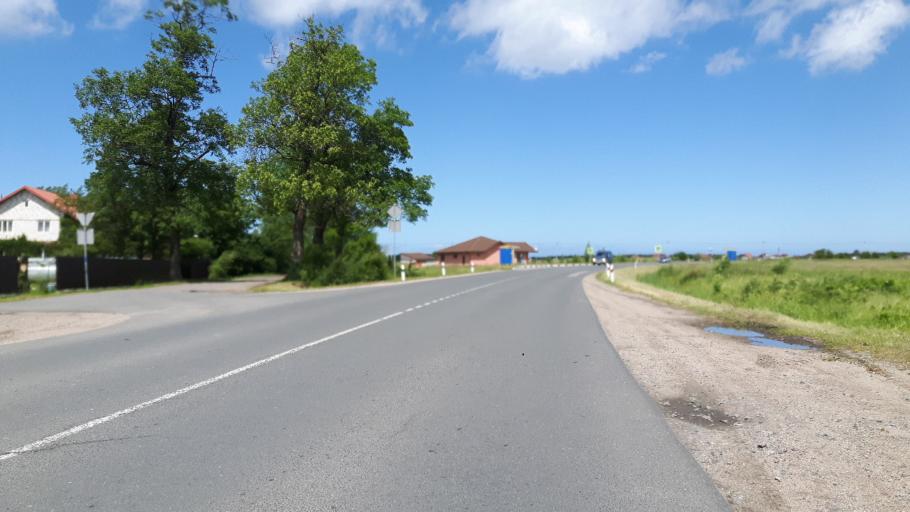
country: RU
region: Kaliningrad
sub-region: Zelenogradskiy Rayon
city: Zelenogradsk
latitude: 54.9258
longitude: 20.3980
